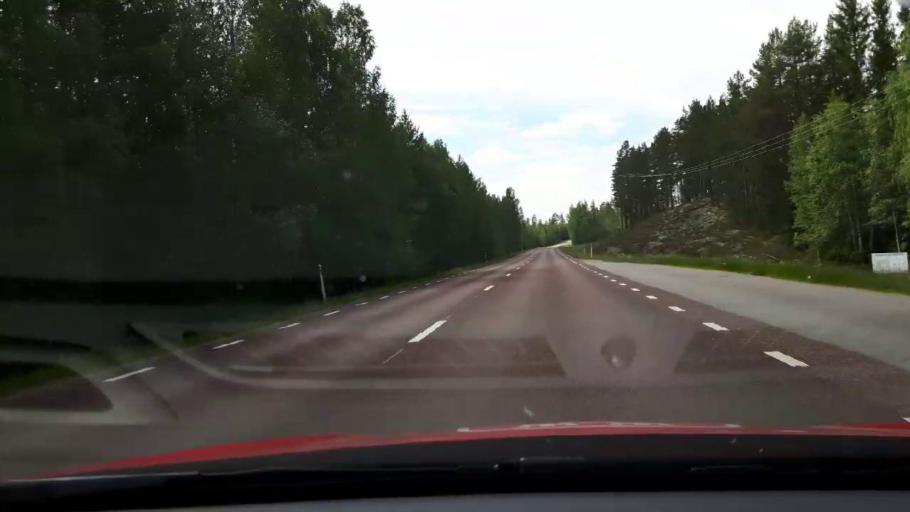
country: SE
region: Jaemtland
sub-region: Harjedalens Kommun
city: Sveg
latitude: 62.0546
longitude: 14.9025
